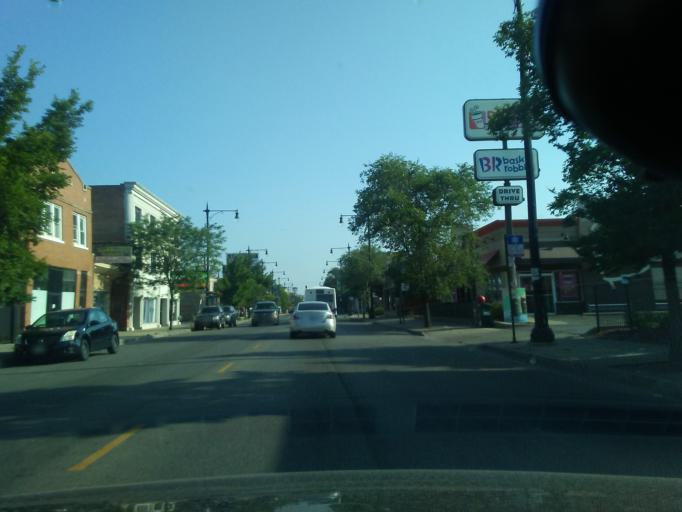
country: US
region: Illinois
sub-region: Cook County
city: Elmwood Park
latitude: 41.9358
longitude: -87.7664
